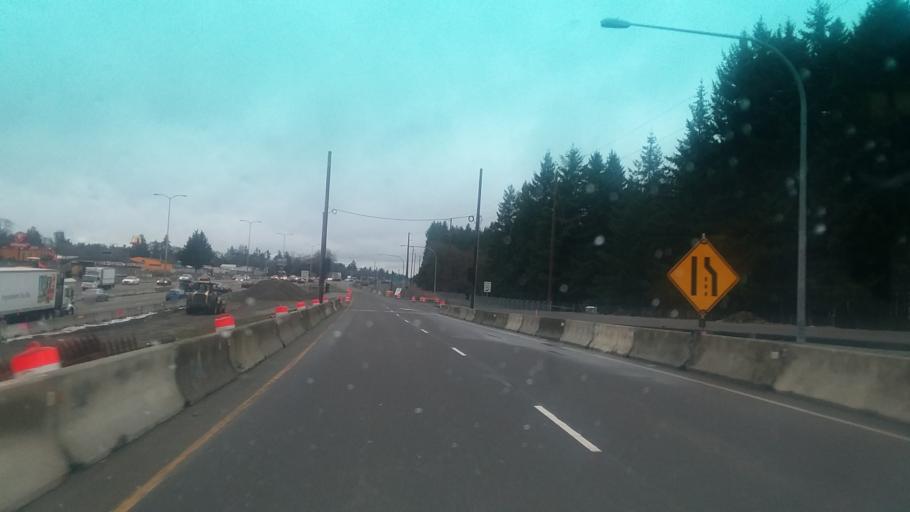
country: US
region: Washington
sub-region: Pierce County
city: Fort Lewis
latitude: 47.1186
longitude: -122.5559
